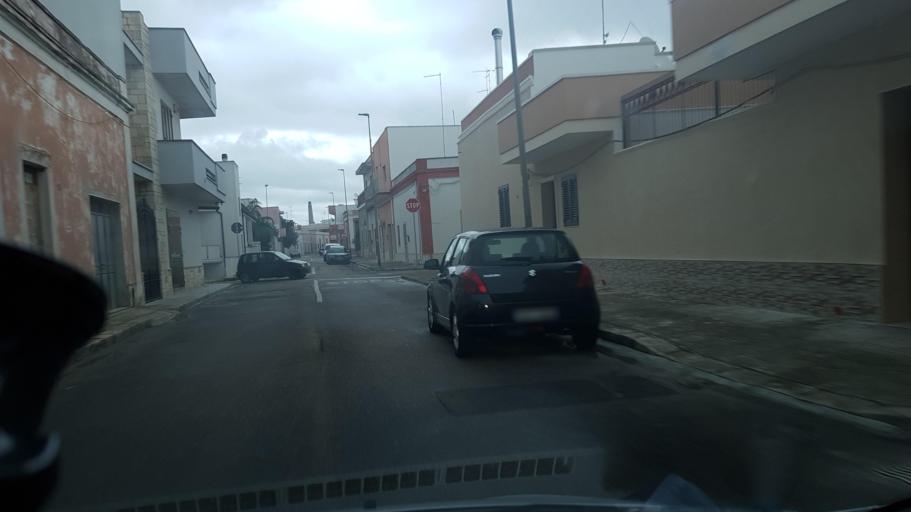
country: IT
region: Apulia
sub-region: Provincia di Lecce
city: Carmiano
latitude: 40.3402
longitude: 18.0437
